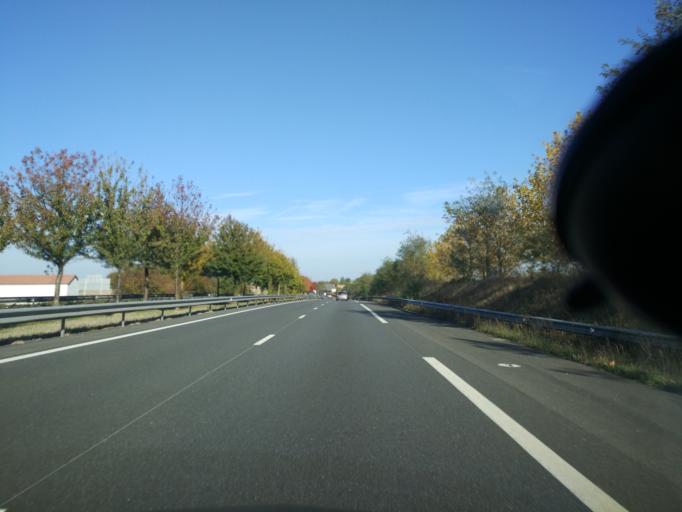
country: FR
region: Poitou-Charentes
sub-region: Departement de la Charente
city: Roullet-Saint-Estephe
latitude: 45.5688
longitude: 0.0241
